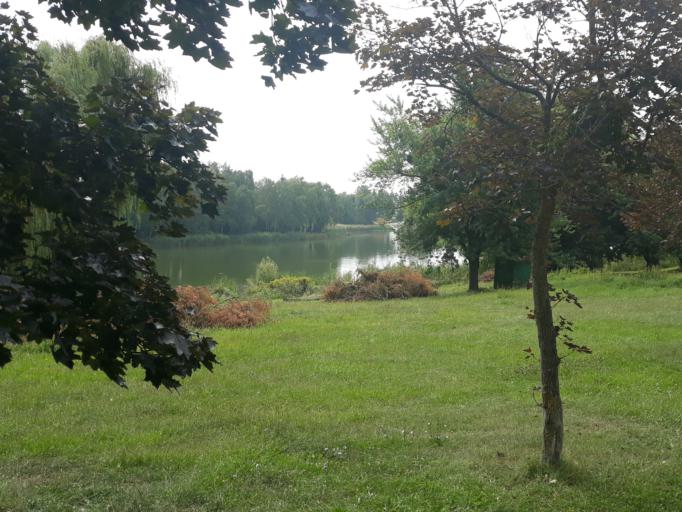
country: HU
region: Zala
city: Zalaegerszeg
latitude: 46.8649
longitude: 16.8173
